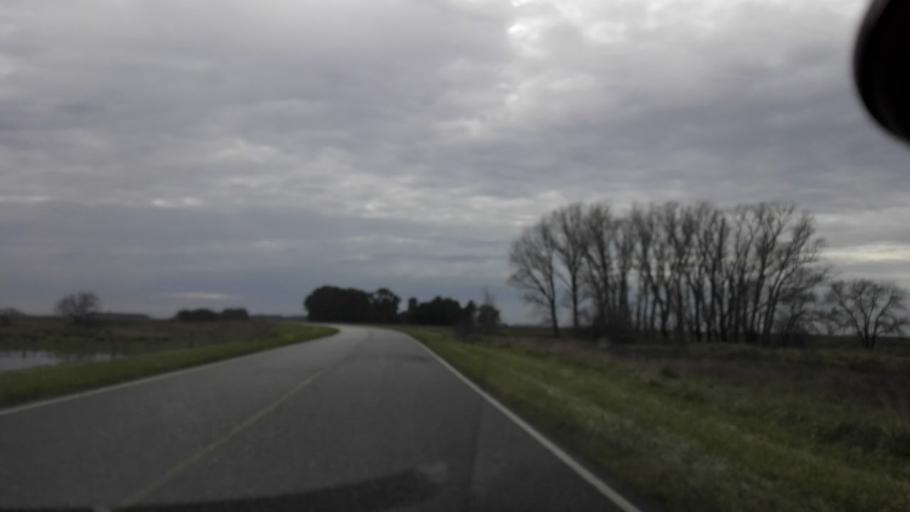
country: AR
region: Buenos Aires
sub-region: Partido de Rauch
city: Rauch
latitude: -36.4573
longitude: -59.0156
